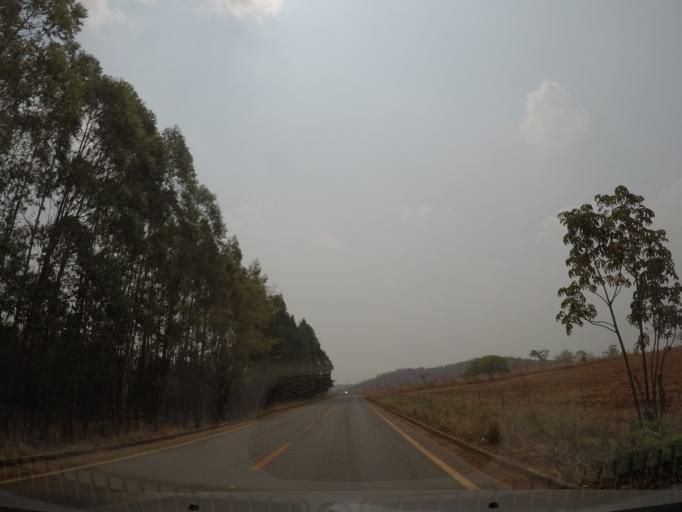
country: BR
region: Goias
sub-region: Pirenopolis
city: Pirenopolis
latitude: -15.9063
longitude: -48.8635
